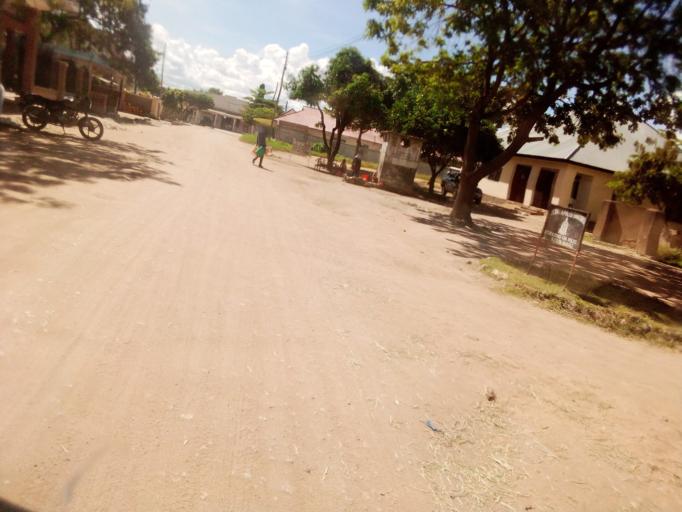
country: TZ
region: Dodoma
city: Dodoma
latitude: -6.1743
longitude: 35.7587
